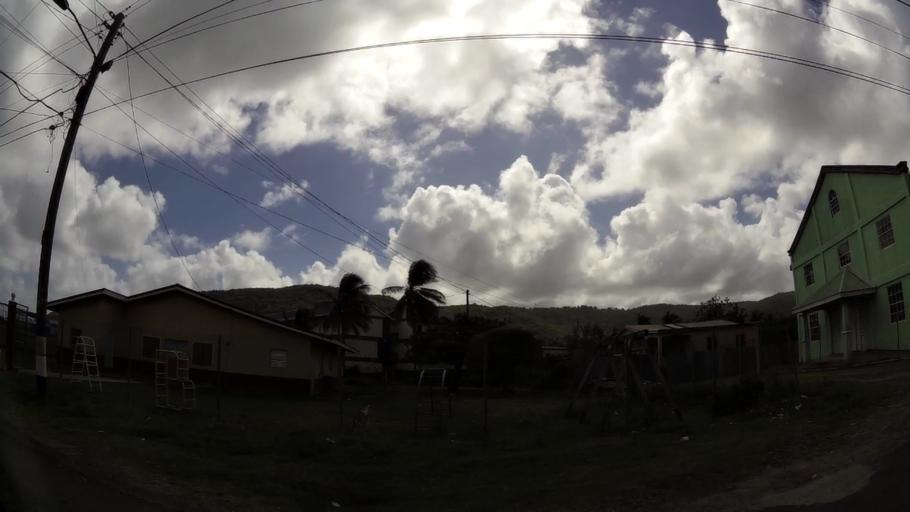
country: LC
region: Dennery Quarter
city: Dennery
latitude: 13.9111
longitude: -60.8928
